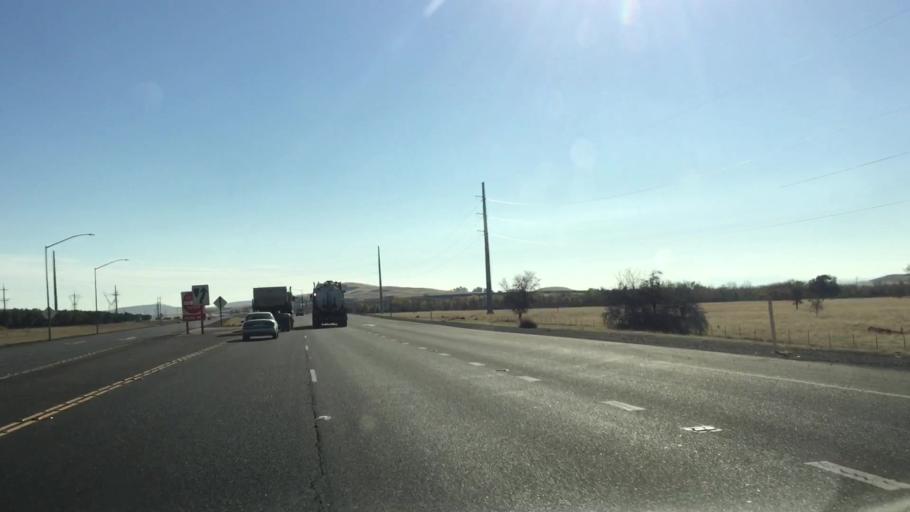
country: US
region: California
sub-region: Butte County
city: Thermalito
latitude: 39.5929
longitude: -121.6204
